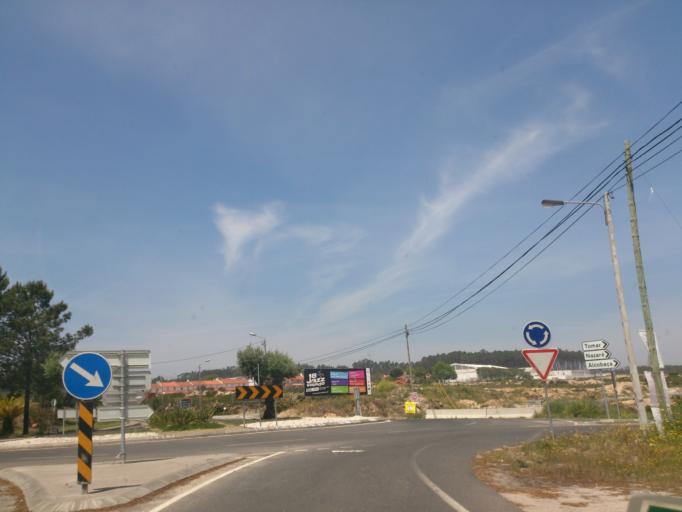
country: PT
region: Leiria
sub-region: Alcobaca
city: Alcobaca
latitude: 39.5871
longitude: -9.0147
